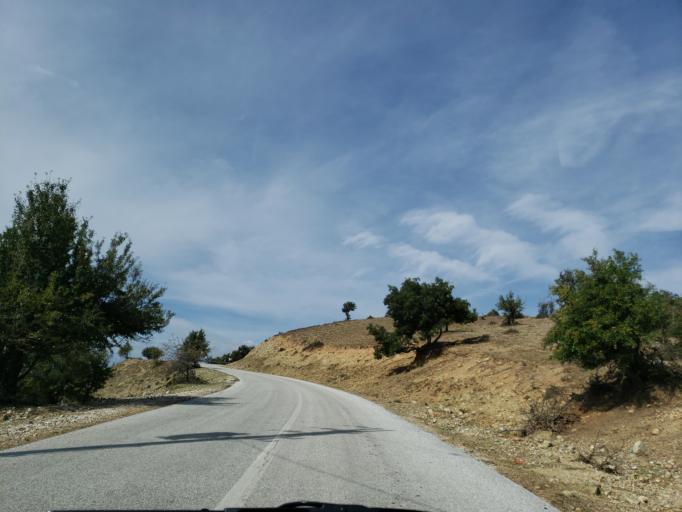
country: GR
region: Thessaly
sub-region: Trikala
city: Kastraki
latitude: 39.7594
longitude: 21.6635
